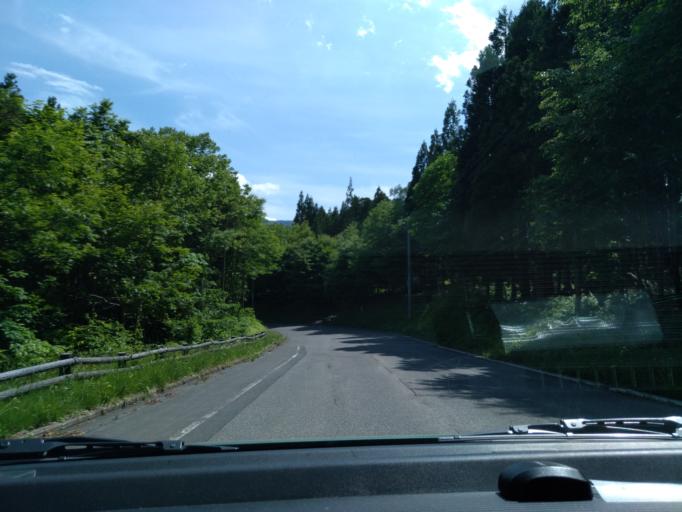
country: JP
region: Iwate
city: Ichinoseki
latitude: 39.0104
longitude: 140.8629
